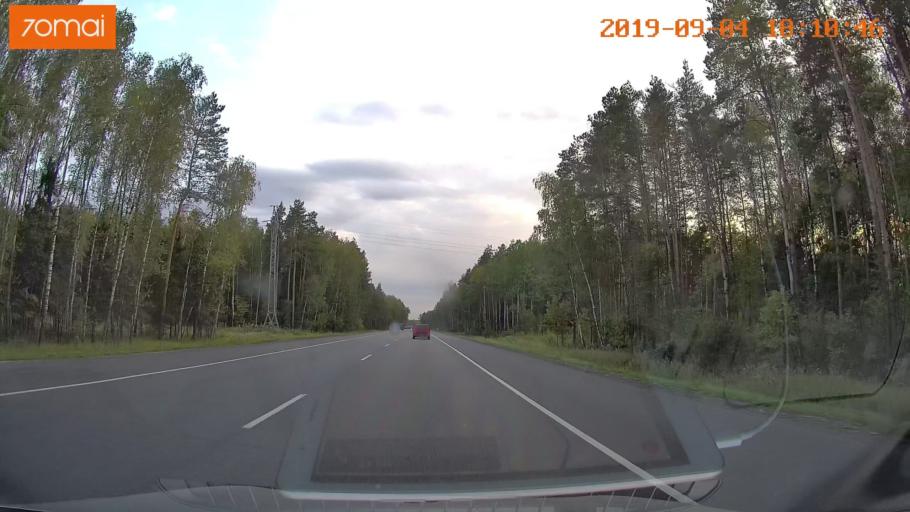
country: RU
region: Moskovskaya
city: Lopatinskiy
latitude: 55.3845
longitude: 38.7617
